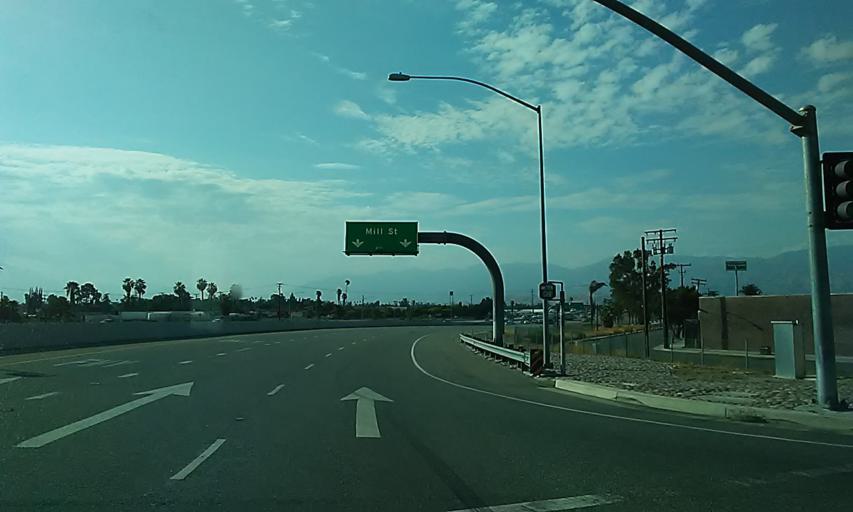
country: US
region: California
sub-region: San Bernardino County
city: Colton
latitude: 34.0857
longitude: -117.3008
